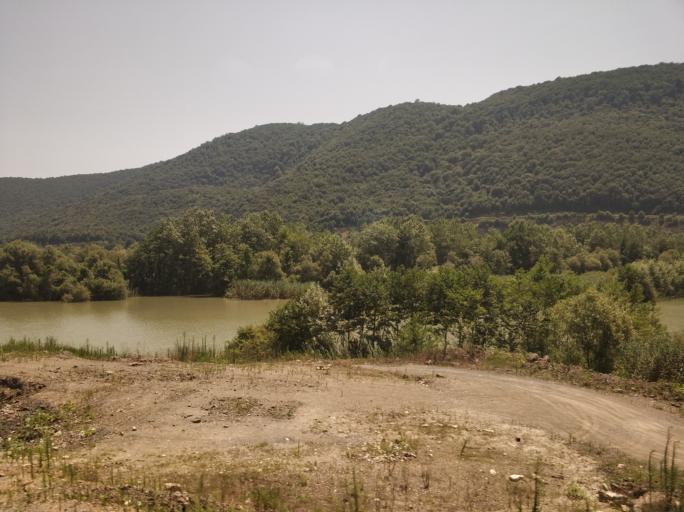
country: IR
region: Gilan
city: Pa'in-e Bazar-e Rudbar
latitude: 36.9860
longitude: 49.5590
